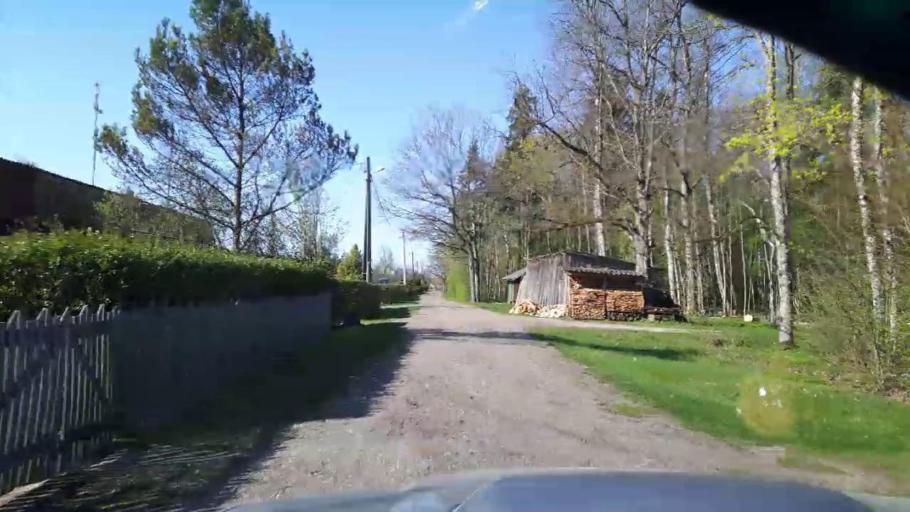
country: EE
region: Paernumaa
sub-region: Sindi linn
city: Sindi
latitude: 58.4514
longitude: 24.7696
